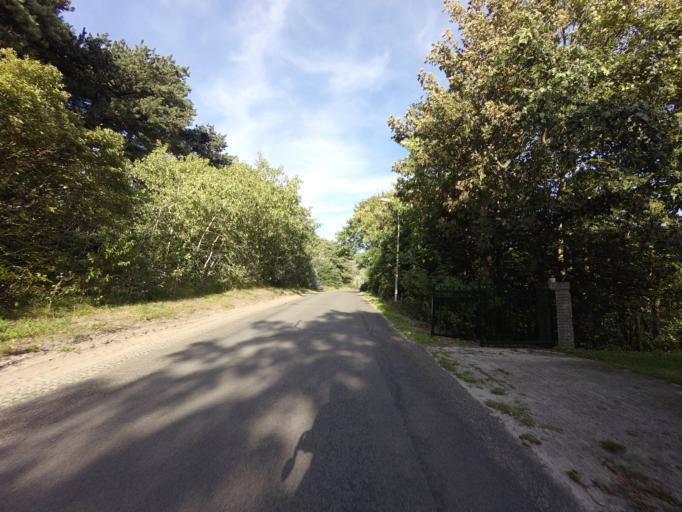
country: NL
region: Friesland
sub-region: Gemeente Ameland
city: Nes
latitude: 53.4538
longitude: 5.7808
